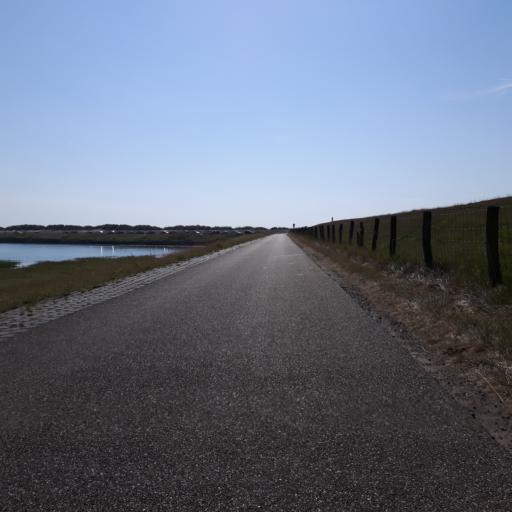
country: NL
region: Zeeland
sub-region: Gemeente Middelburg
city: Middelburg
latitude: 51.4541
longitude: 3.6551
